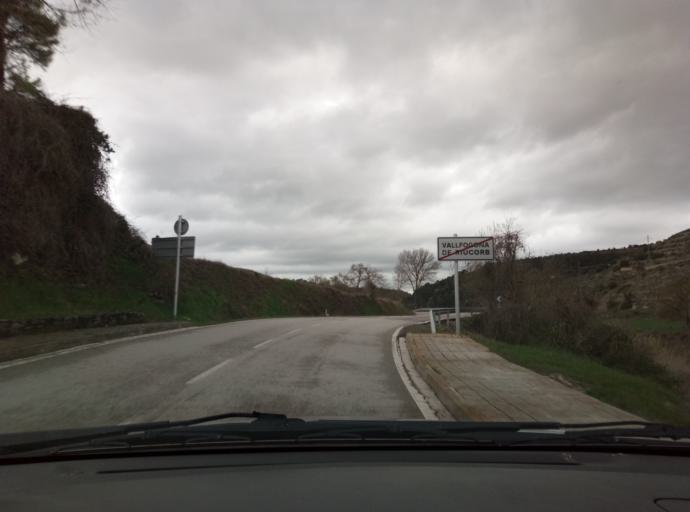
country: ES
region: Catalonia
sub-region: Provincia de Tarragona
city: Vallfogona de Riucorb
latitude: 41.5633
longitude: 1.2347
